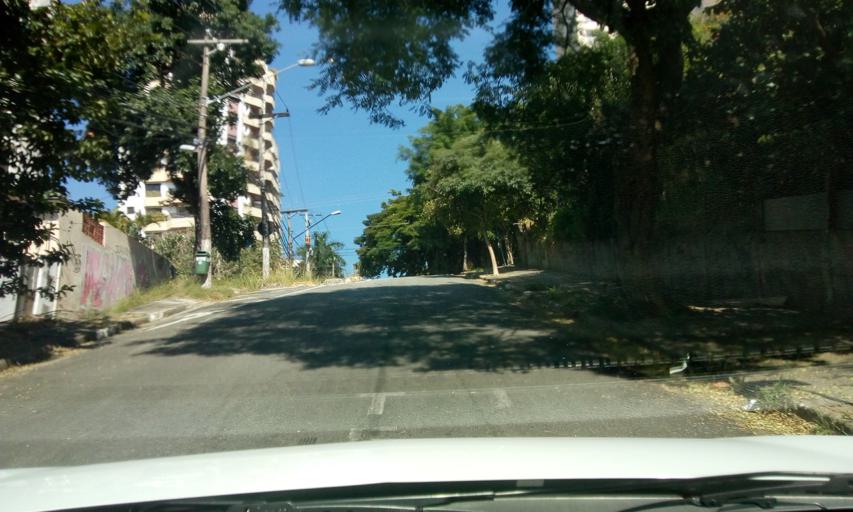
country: BR
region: Sao Paulo
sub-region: Sao Paulo
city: Sao Paulo
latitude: -23.5404
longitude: -46.6850
